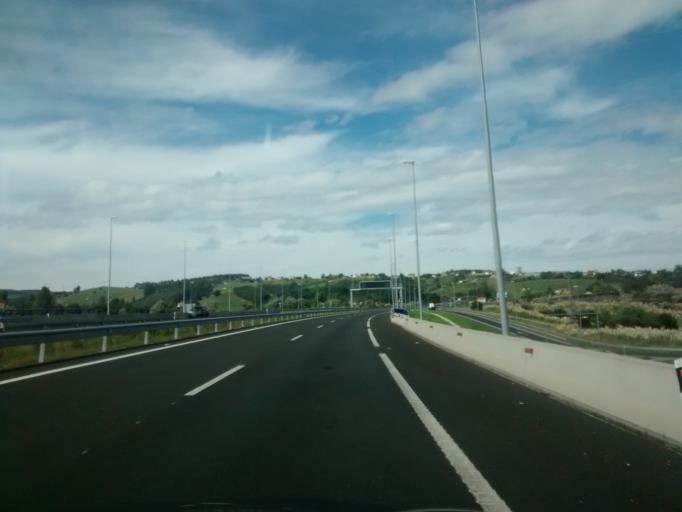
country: ES
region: Cantabria
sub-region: Provincia de Cantabria
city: Camargo
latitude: 43.3846
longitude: -3.8568
